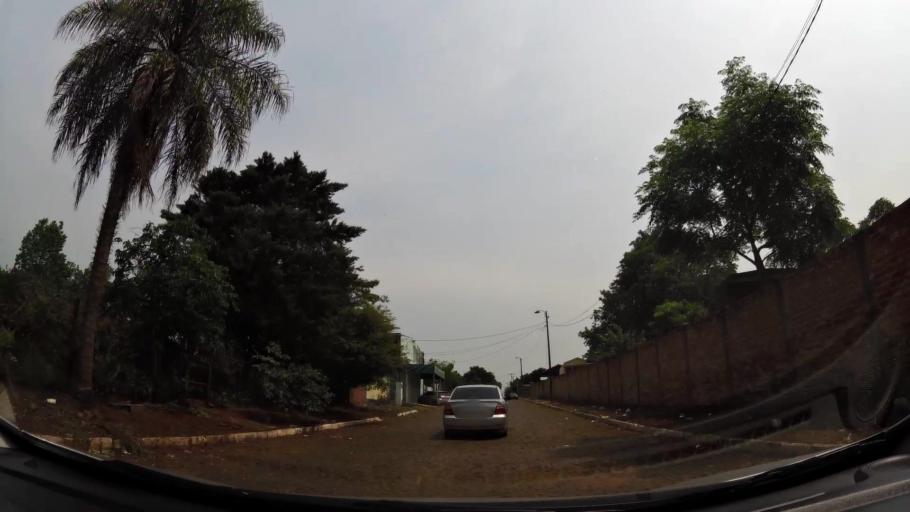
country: BR
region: Parana
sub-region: Foz Do Iguacu
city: Foz do Iguacu
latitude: -25.5677
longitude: -54.6079
